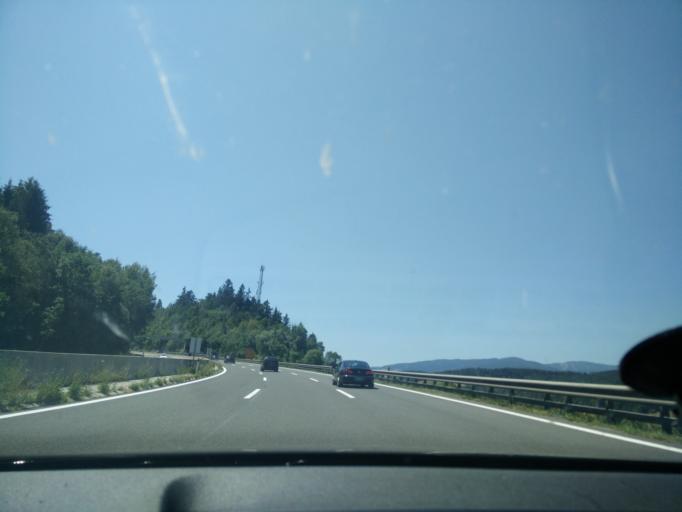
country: AT
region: Lower Austria
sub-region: Politischer Bezirk Neunkirchen
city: Edlitz
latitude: 47.5872
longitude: 16.1086
